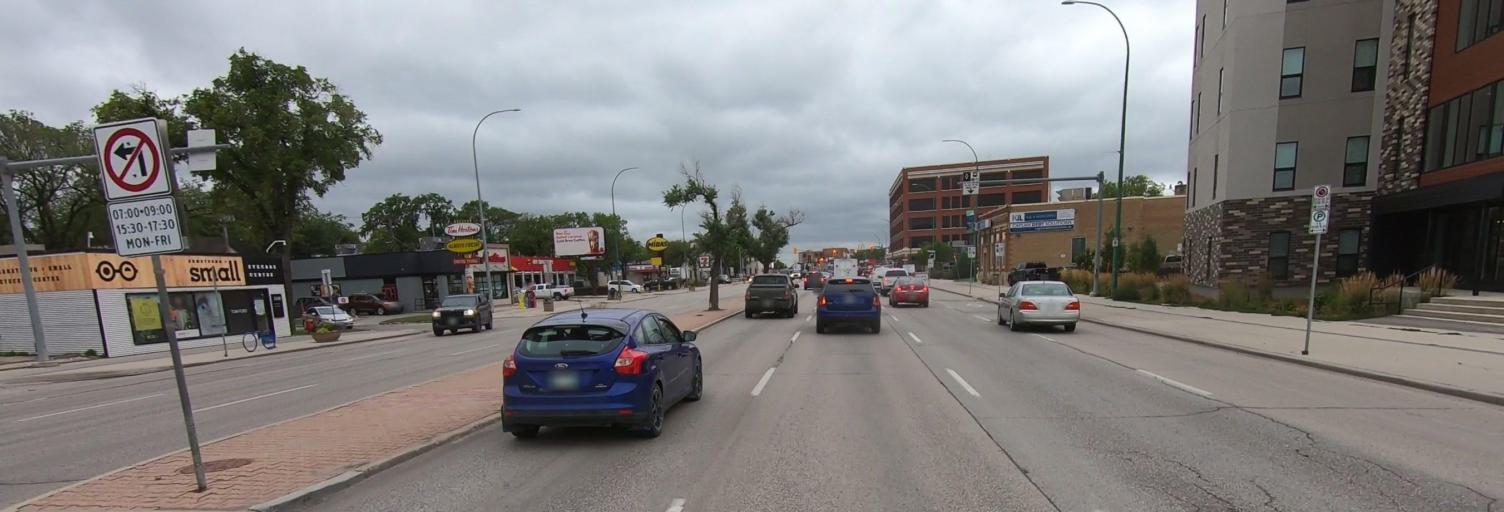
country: CA
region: Manitoba
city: Winnipeg
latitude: 49.8840
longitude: -97.1805
